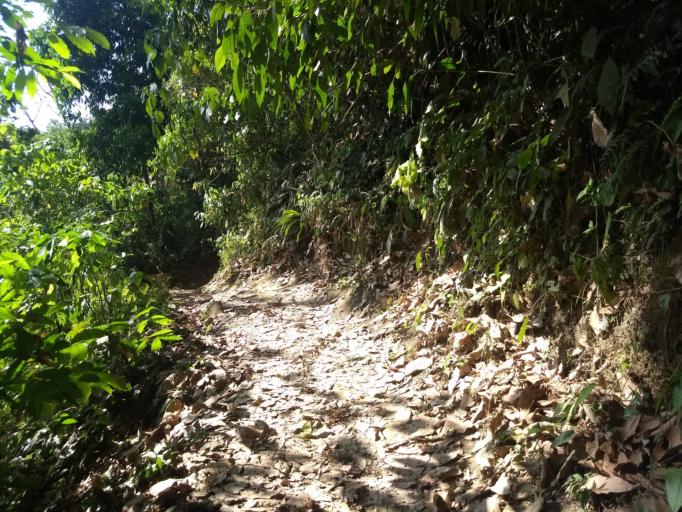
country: CO
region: Magdalena
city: Santa Marta
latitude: 11.1461
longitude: -74.1079
